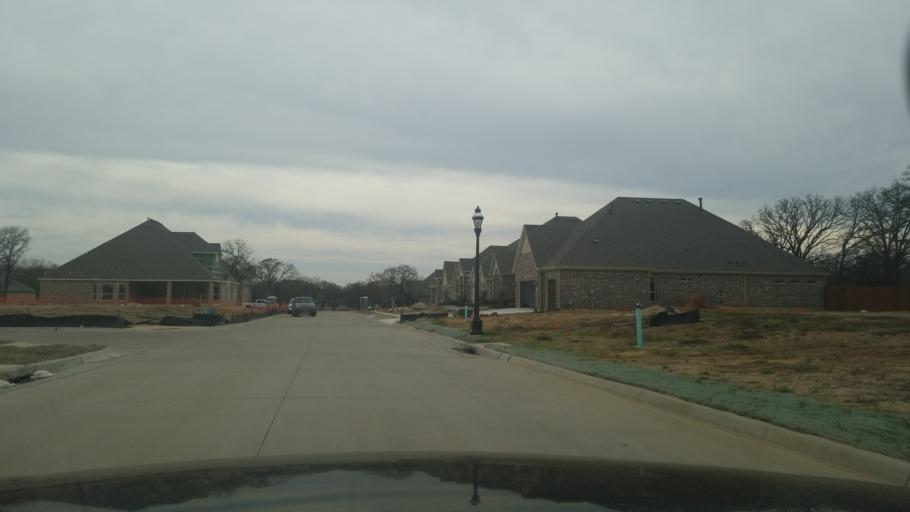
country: US
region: Texas
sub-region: Denton County
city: Corinth
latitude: 33.1338
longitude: -97.0783
